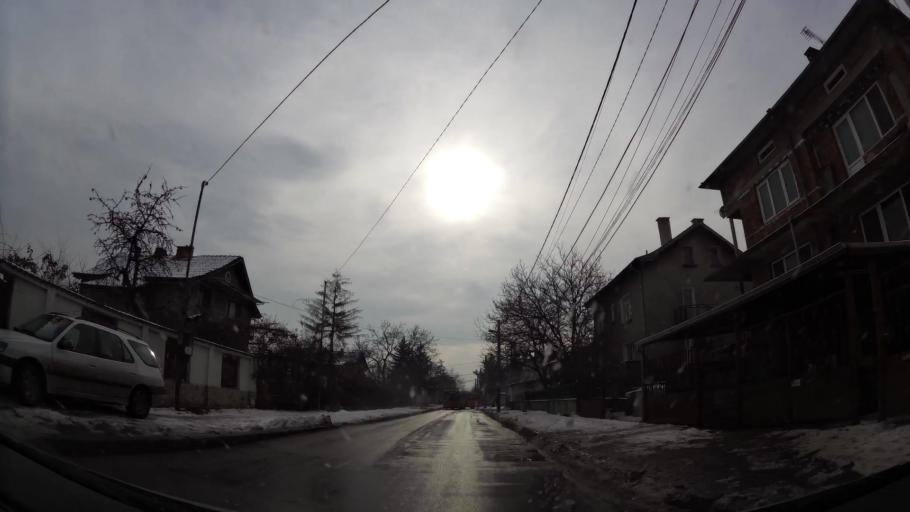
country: BG
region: Sofia-Capital
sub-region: Stolichna Obshtina
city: Sofia
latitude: 42.7109
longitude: 23.4027
